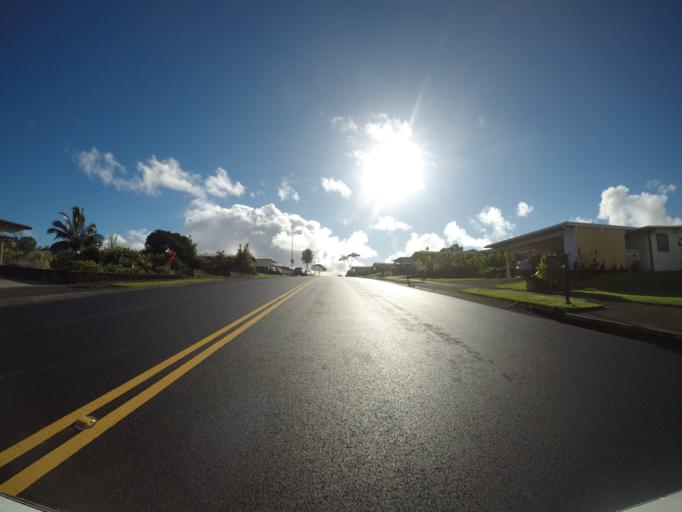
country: US
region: Hawaii
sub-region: Honolulu County
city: He'eia
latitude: 21.4238
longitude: -157.8090
